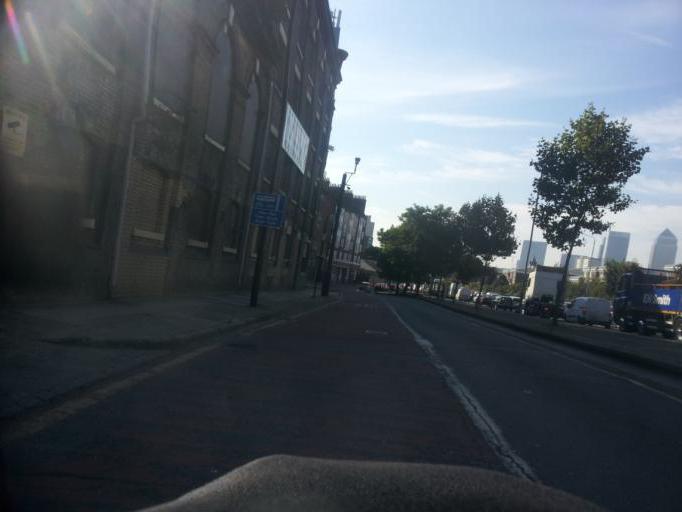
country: GB
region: England
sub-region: Greater London
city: Poplar
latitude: 51.5209
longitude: -0.0101
